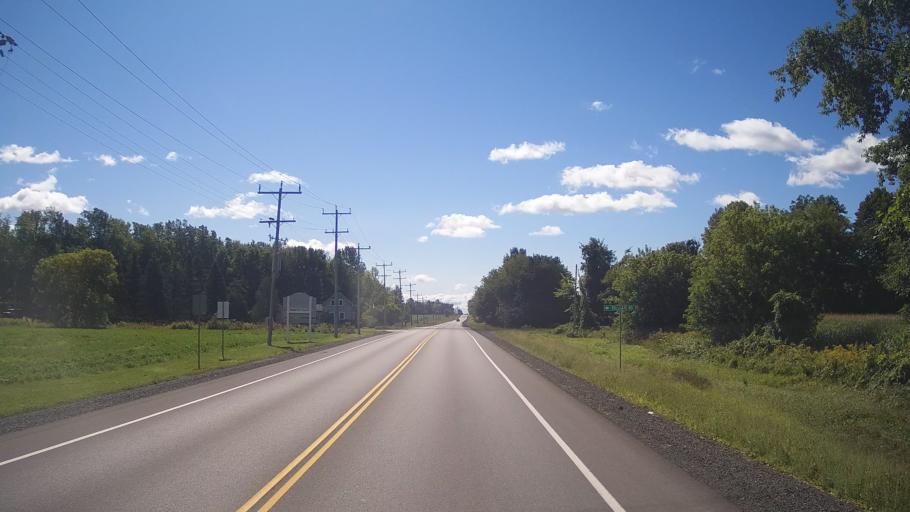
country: US
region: New York
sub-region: St. Lawrence County
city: Norfolk
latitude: 44.9690
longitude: -75.2391
